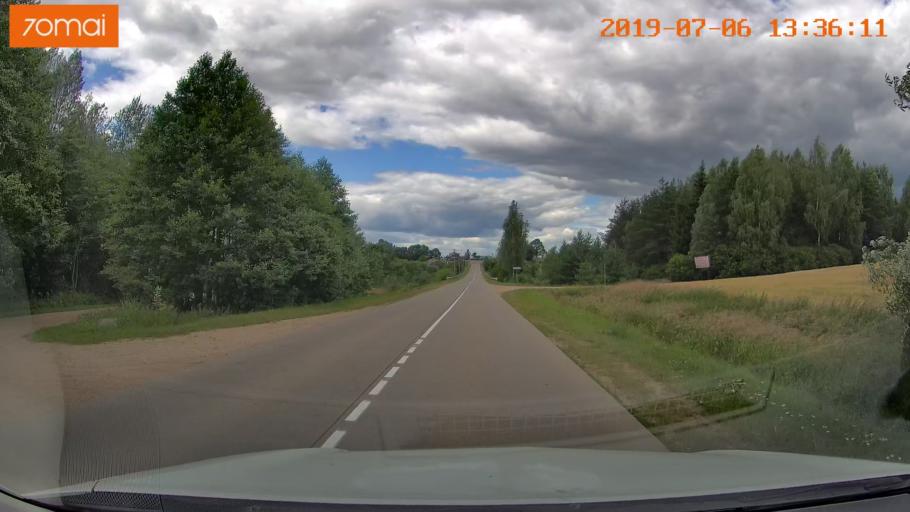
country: BY
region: Minsk
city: Enyerhyetykaw
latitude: 53.6876
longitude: 26.8695
